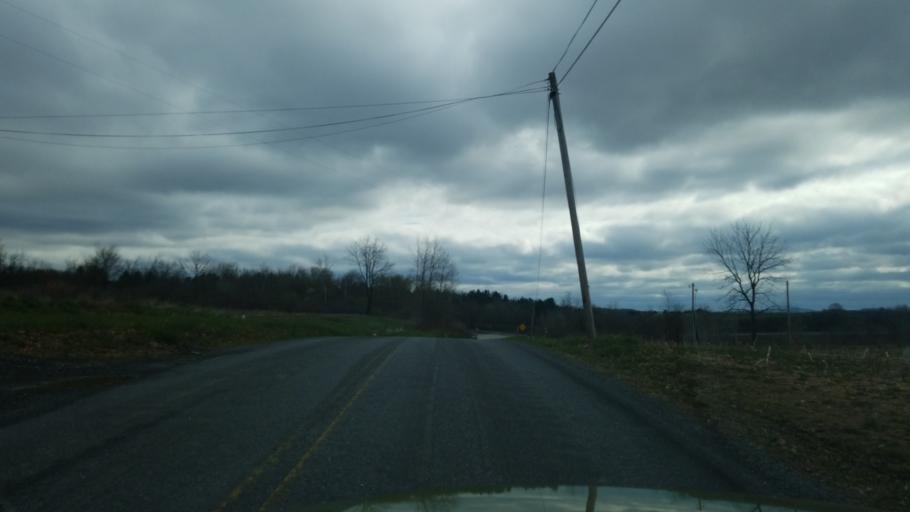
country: US
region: Pennsylvania
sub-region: Clearfield County
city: Clearfield
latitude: 41.0509
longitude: -78.4316
